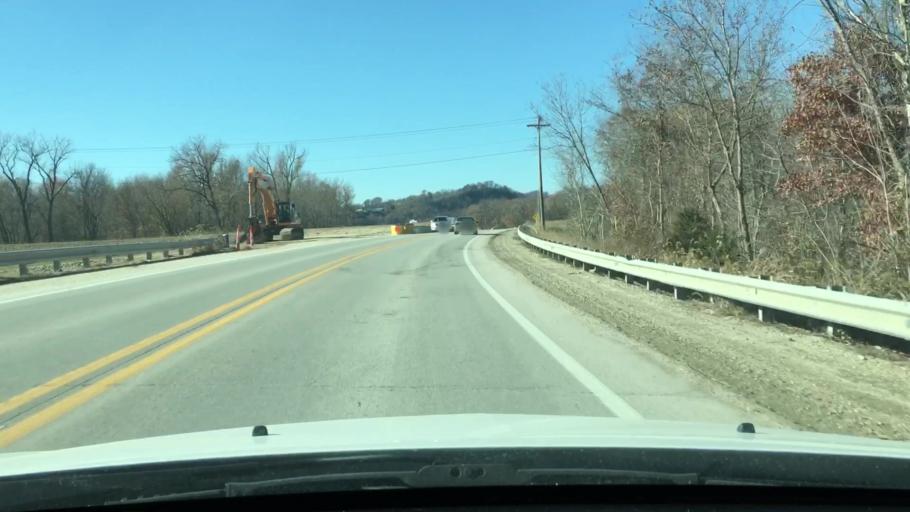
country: US
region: Missouri
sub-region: Pike County
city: Louisiana
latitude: 39.4600
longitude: -91.0358
